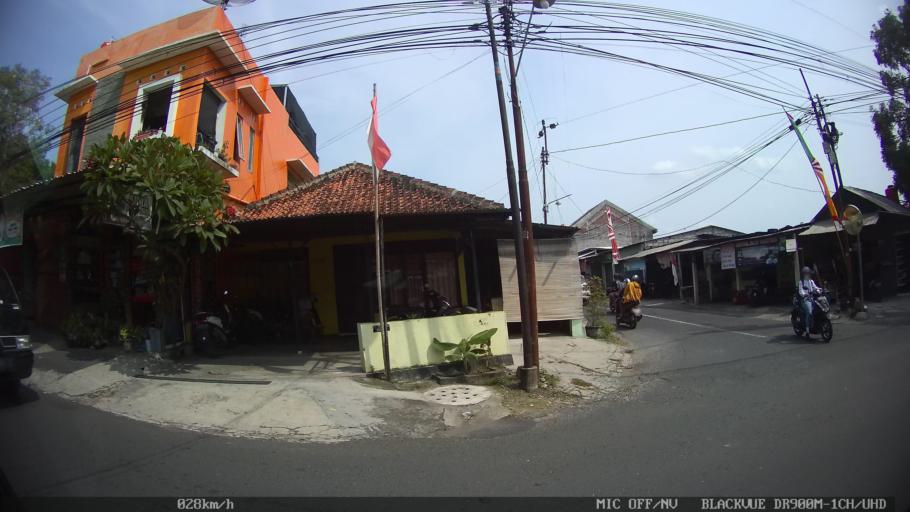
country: ID
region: Daerah Istimewa Yogyakarta
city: Depok
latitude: -7.8030
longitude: 110.4203
